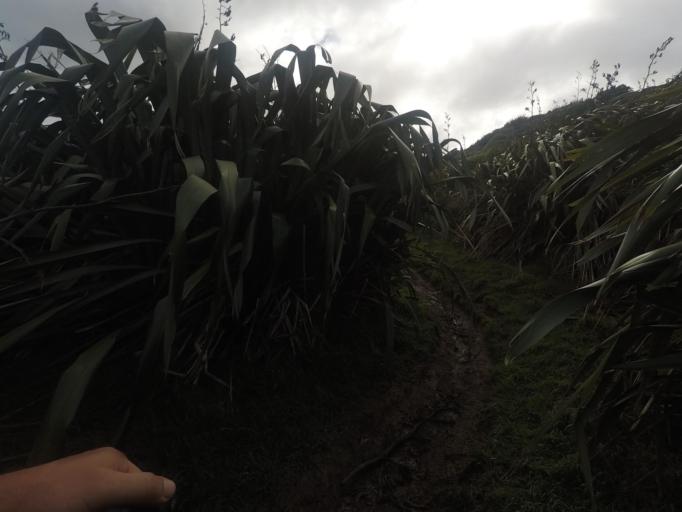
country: NZ
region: Auckland
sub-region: Auckland
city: Muriwai Beach
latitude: -36.8721
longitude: 174.4334
